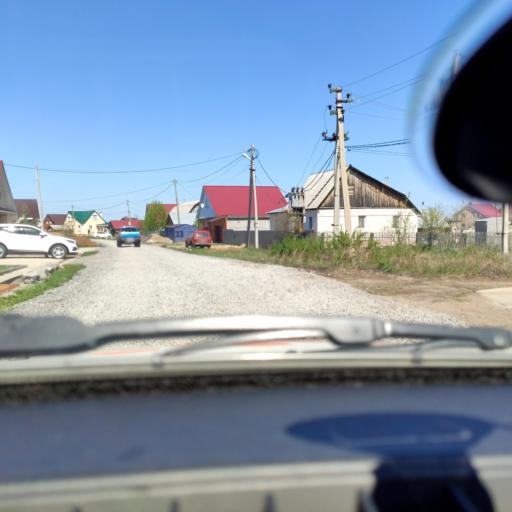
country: RU
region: Bashkortostan
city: Iglino
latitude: 54.7951
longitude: 56.2793
